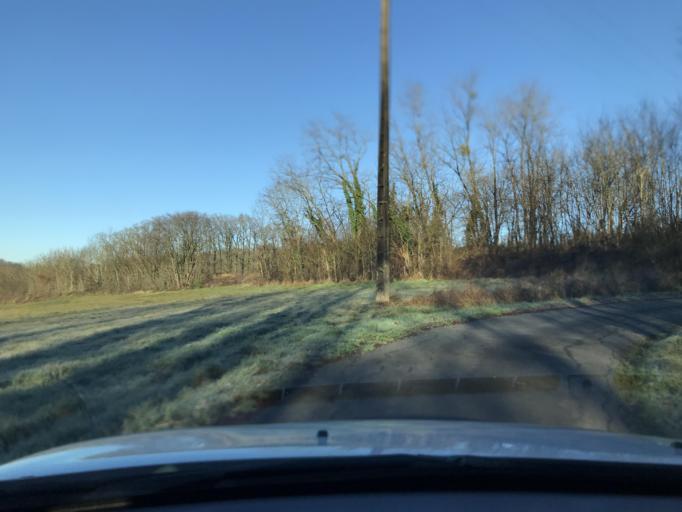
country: FR
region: Poitou-Charentes
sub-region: Departement de la Charente
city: Chasseneuil-sur-Bonnieure
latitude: 45.8361
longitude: 0.5027
